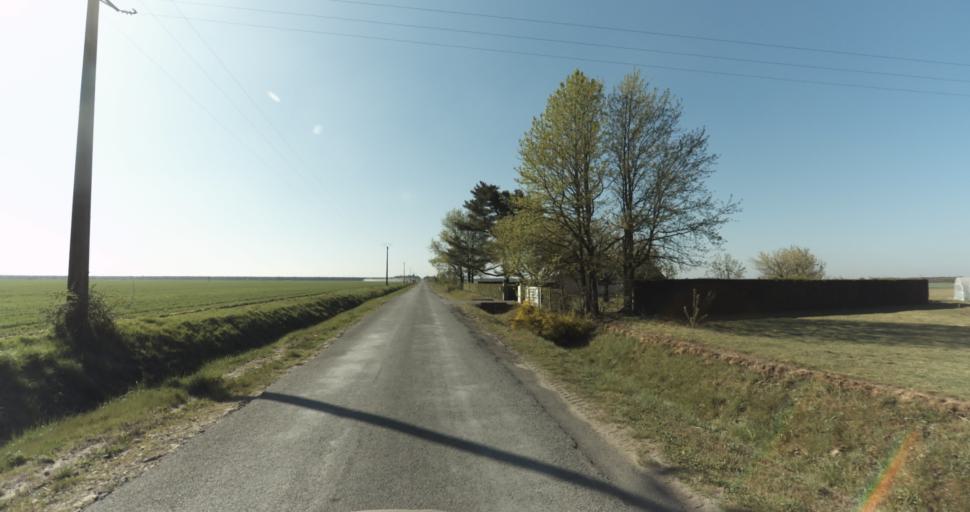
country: FR
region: Aquitaine
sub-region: Departement de la Gironde
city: Marcheprime
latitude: 44.7746
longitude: -0.8584
